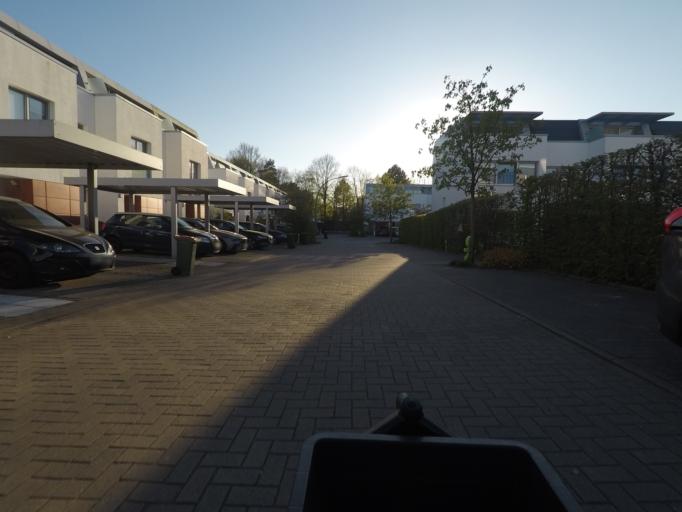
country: DE
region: Hamburg
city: Marienthal
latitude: 53.5626
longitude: 10.0769
